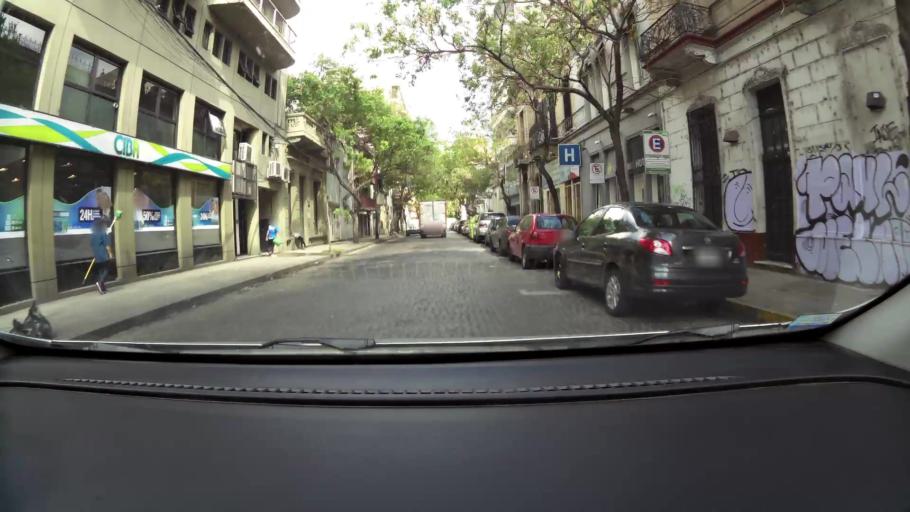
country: AR
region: Santa Fe
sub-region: Departamento de Rosario
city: Rosario
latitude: -32.9542
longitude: -60.6447
